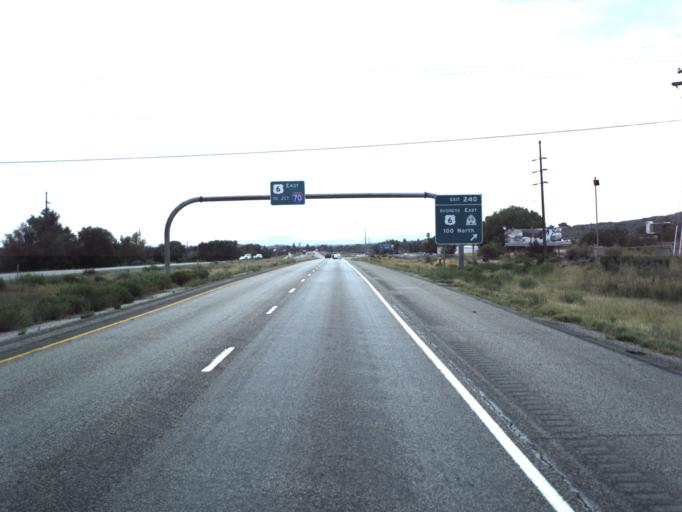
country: US
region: Utah
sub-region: Carbon County
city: Carbonville
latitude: 39.6099
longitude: -110.8348
